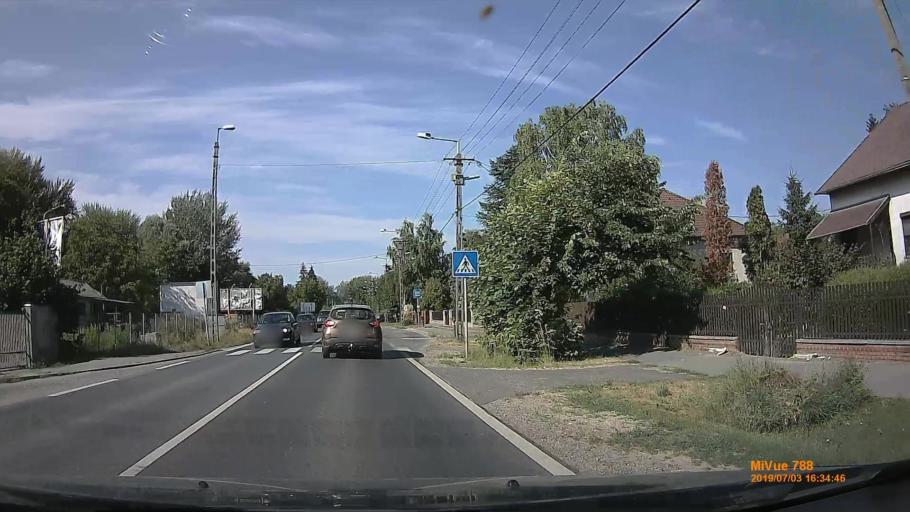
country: HU
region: Gyor-Moson-Sopron
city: Gyor
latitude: 47.7100
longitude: 17.6353
